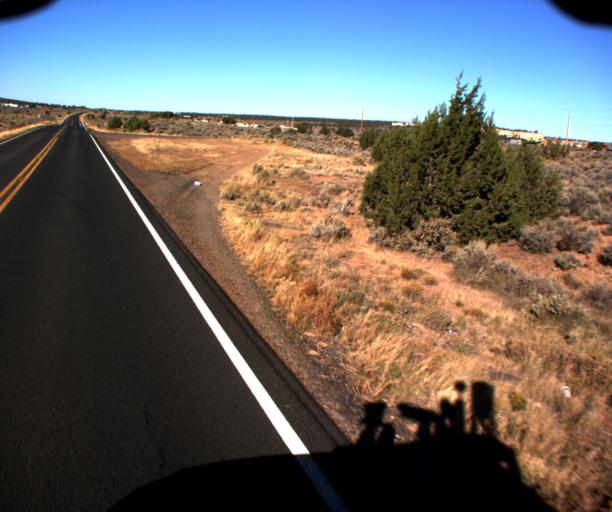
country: US
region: Arizona
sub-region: Apache County
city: Ganado
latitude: 35.7605
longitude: -109.7641
